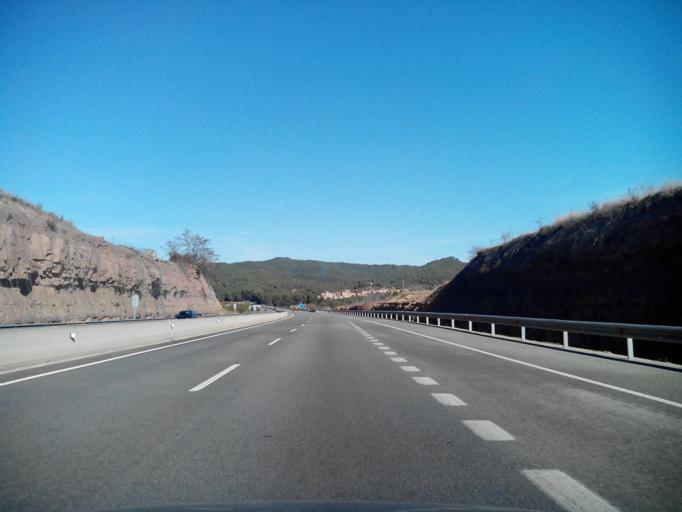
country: ES
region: Catalonia
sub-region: Provincia de Barcelona
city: Navas
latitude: 41.9048
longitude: 1.8753
